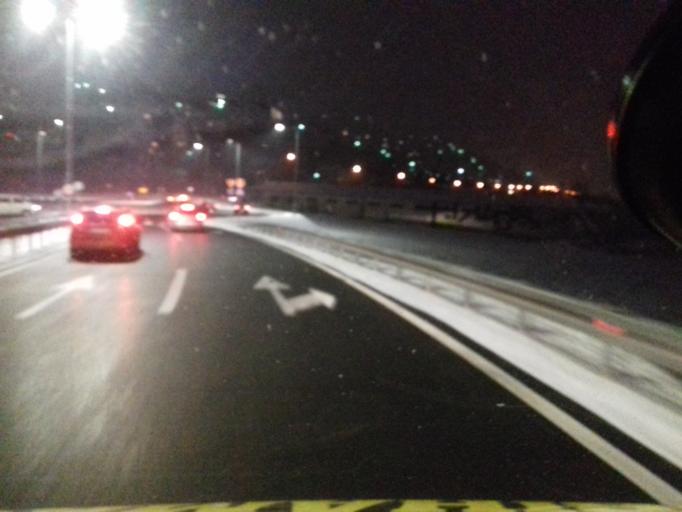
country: BA
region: Federation of Bosnia and Herzegovina
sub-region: Kanton Sarajevo
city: Sarajevo
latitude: 43.8516
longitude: 18.3369
